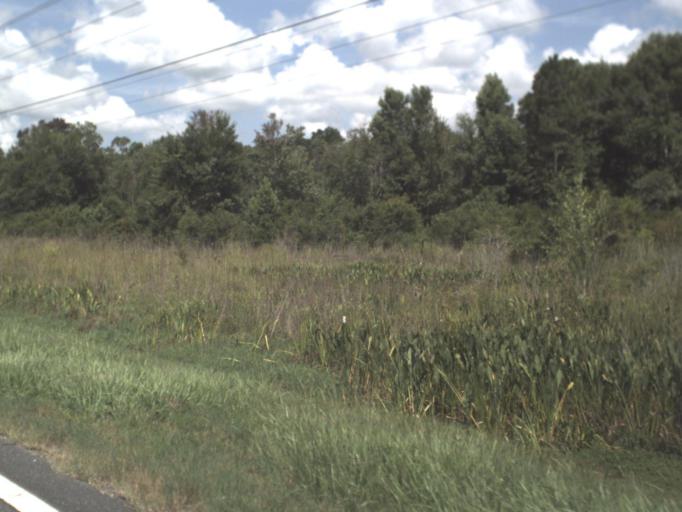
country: US
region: Florida
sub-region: Levy County
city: Chiefland
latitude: 29.2572
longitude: -82.8939
